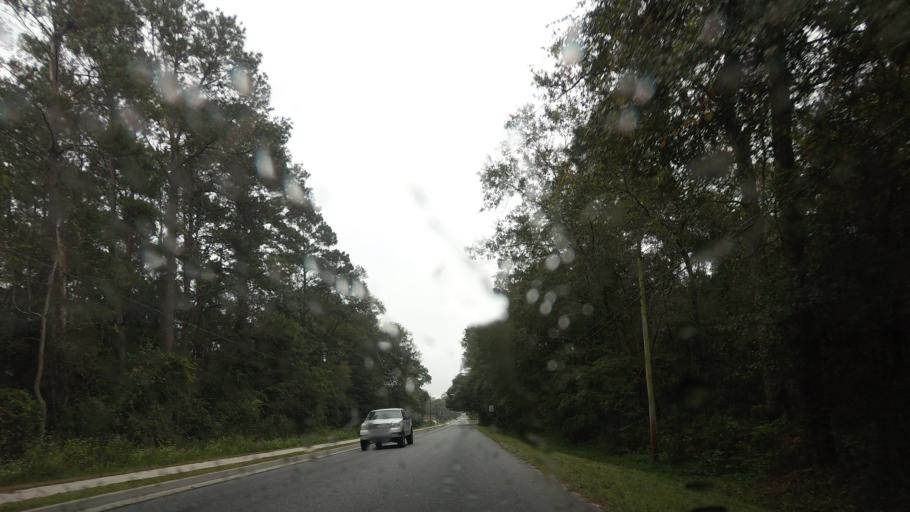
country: US
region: Georgia
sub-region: Lowndes County
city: Remerton
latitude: 30.8295
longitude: -83.3037
